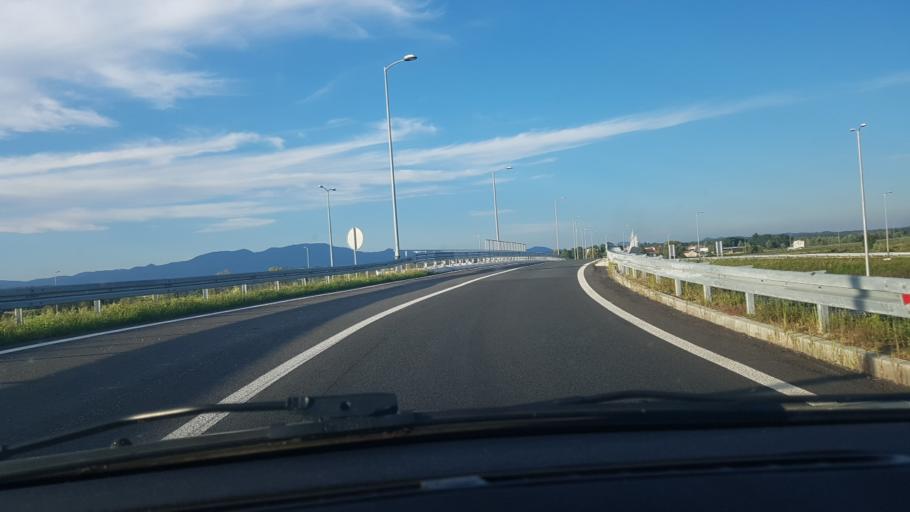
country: HR
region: Krapinsko-Zagorska
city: Selnica
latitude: 46.0367
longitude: 16.0740
